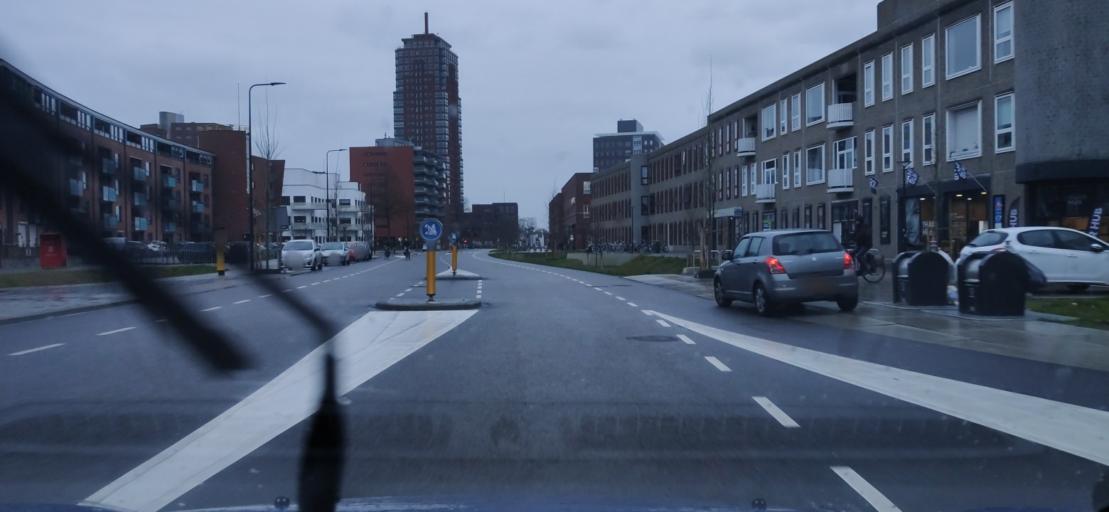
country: NL
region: Overijssel
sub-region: Gemeente Enschede
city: Enschede
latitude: 52.2197
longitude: 6.9001
